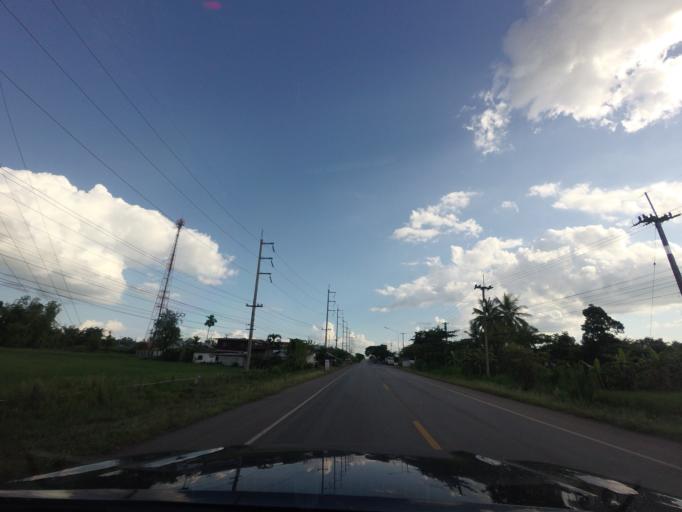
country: TH
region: Changwat Udon Thani
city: Thung Fon
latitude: 17.5090
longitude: 103.2034
